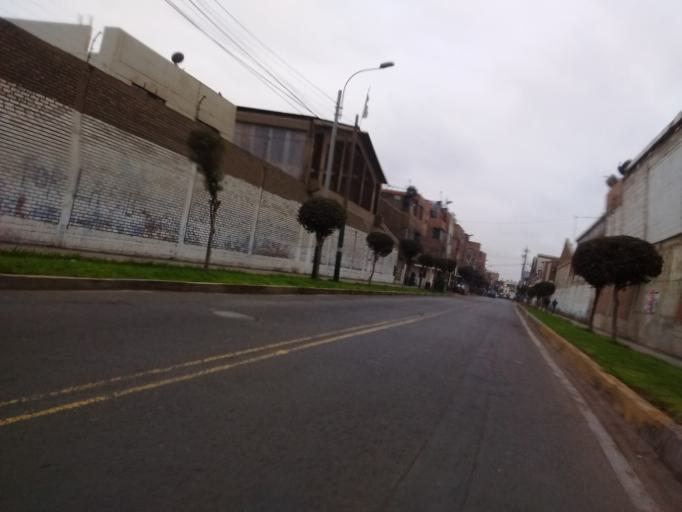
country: PE
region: Callao
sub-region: Callao
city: Callao
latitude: -12.0447
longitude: -77.0856
